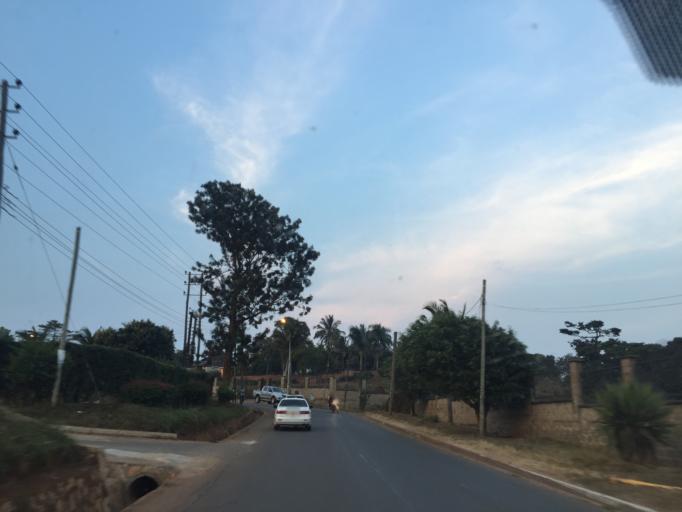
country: UG
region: Central Region
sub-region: Kampala District
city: Kampala
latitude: 0.2423
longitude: 32.6272
